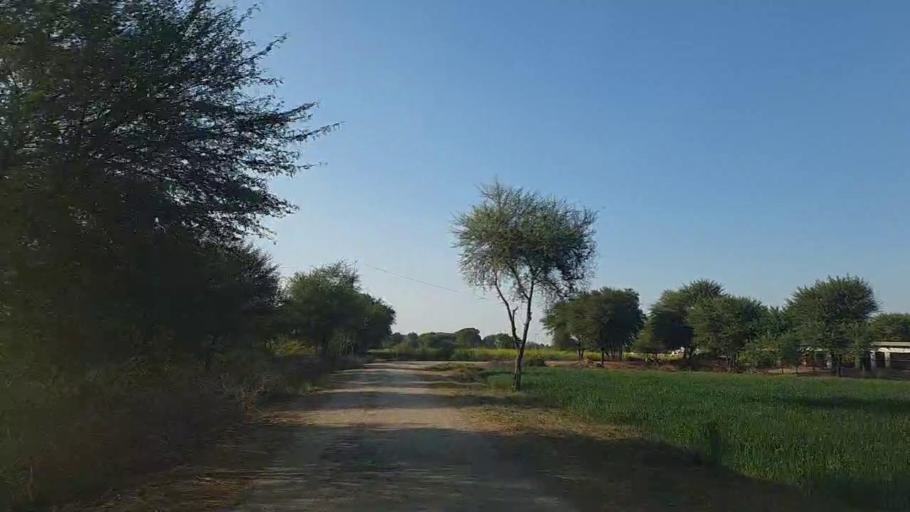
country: PK
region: Sindh
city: Shahpur Chakar
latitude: 26.1946
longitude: 68.6340
